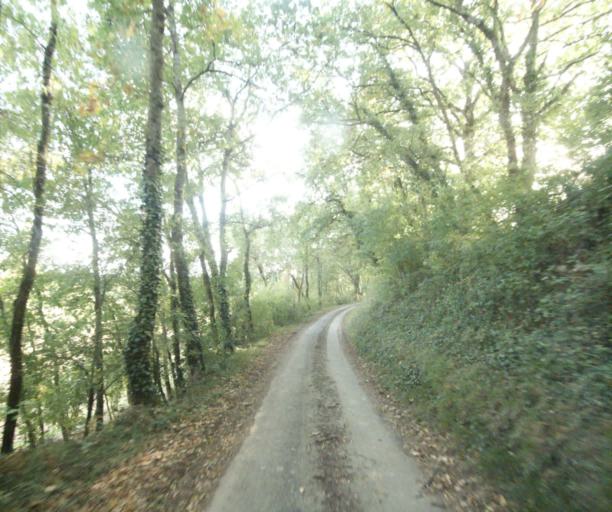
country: FR
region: Midi-Pyrenees
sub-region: Departement du Gers
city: Gondrin
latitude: 43.9039
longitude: 0.2896
